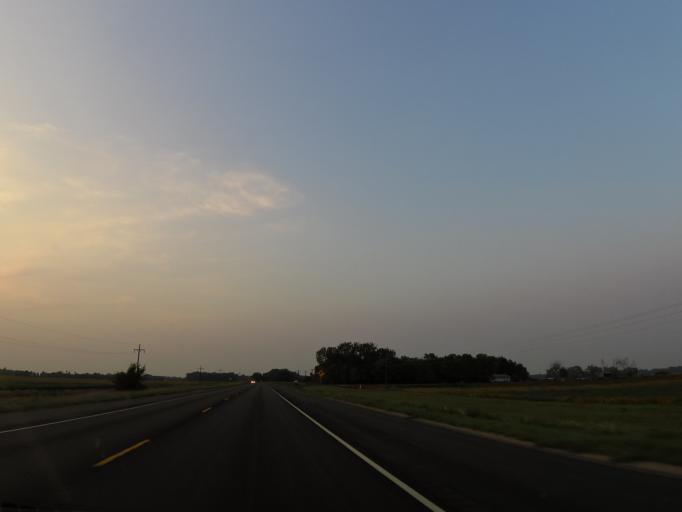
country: US
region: North Dakota
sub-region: Walsh County
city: Park River
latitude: 48.4040
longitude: -97.6228
